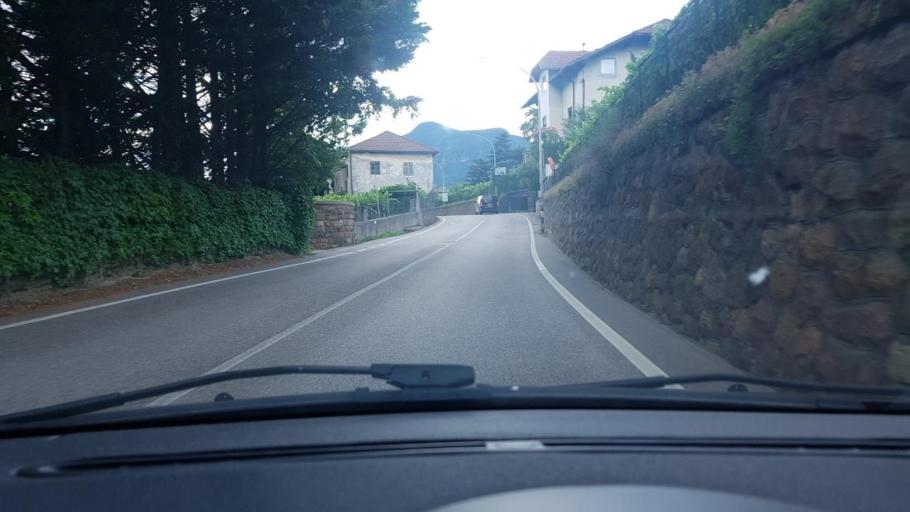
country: IT
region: Trentino-Alto Adige
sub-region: Bolzano
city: Cardano
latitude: 46.4966
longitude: 11.3823
